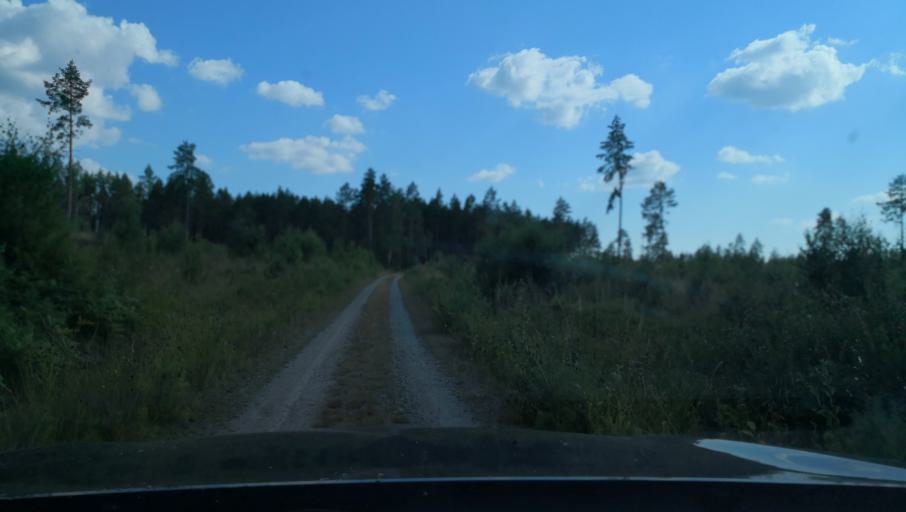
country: SE
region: Vaestmanland
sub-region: Vasteras
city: Skultuna
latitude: 59.7220
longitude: 16.3839
